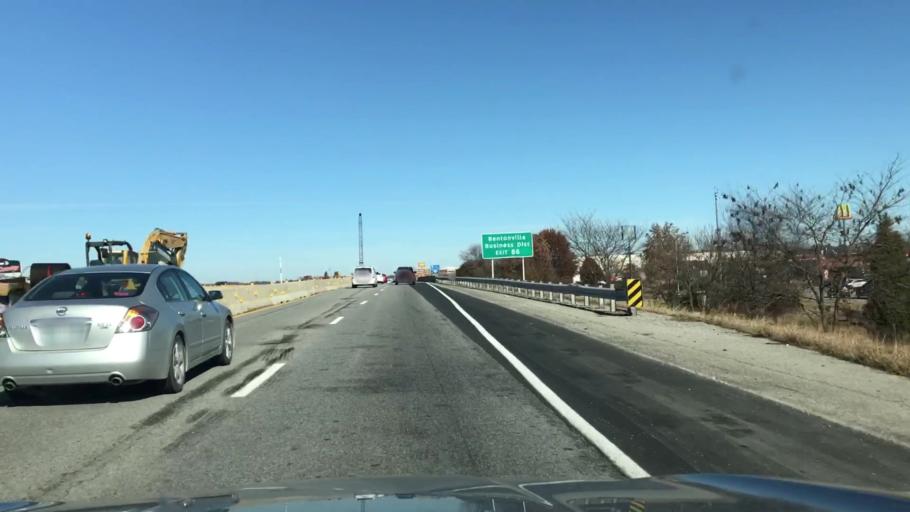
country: US
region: Arkansas
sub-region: Benton County
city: Bentonville
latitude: 36.3340
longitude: -94.1836
